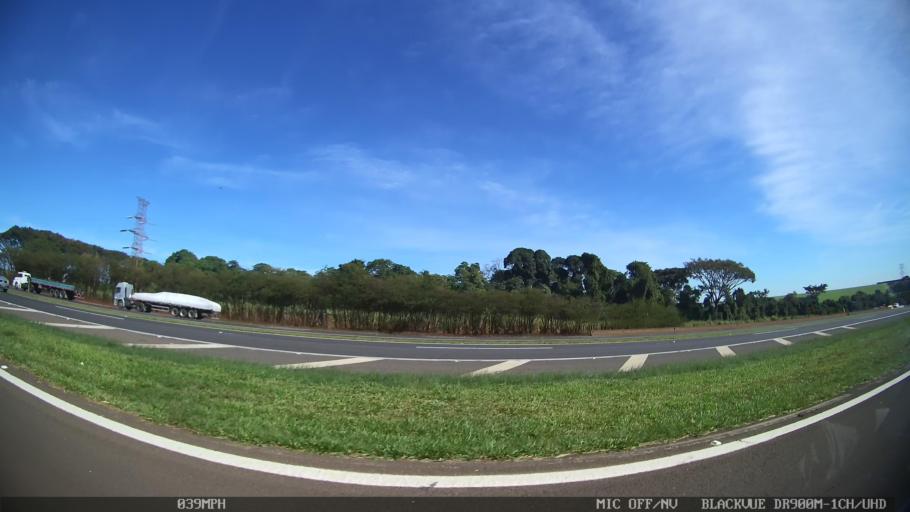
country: BR
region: Sao Paulo
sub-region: Araras
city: Araras
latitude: -22.3144
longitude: -47.3905
